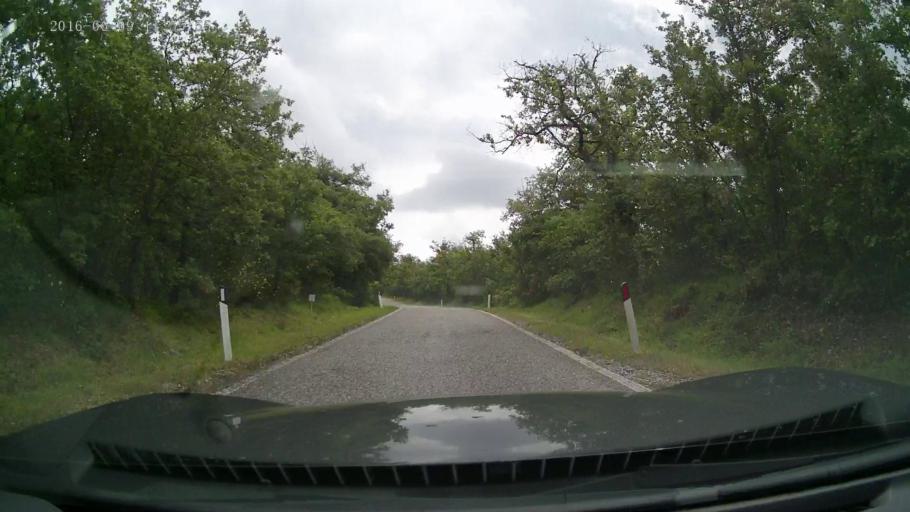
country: IT
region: Tuscany
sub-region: Province of Florence
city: Panzano in Chianti
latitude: 43.5628
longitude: 11.2932
